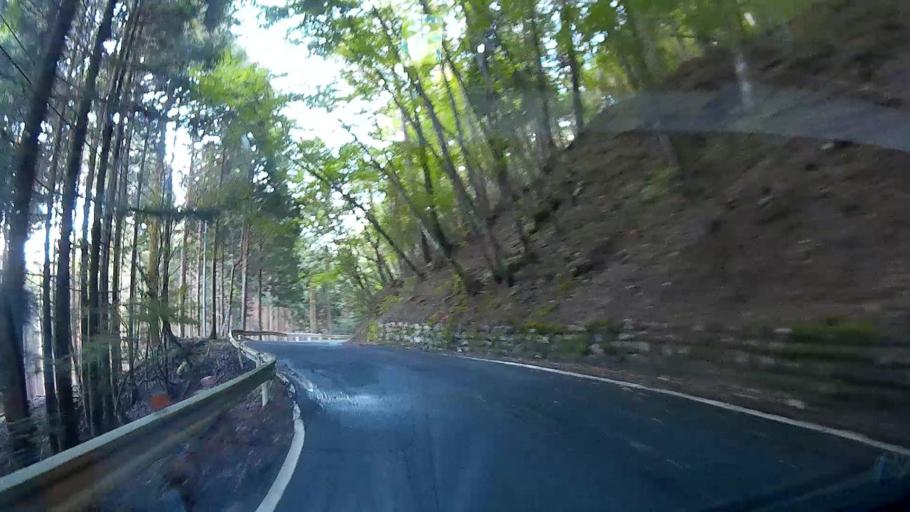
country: JP
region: Shizuoka
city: Shizuoka-shi
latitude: 35.1749
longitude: 138.2508
